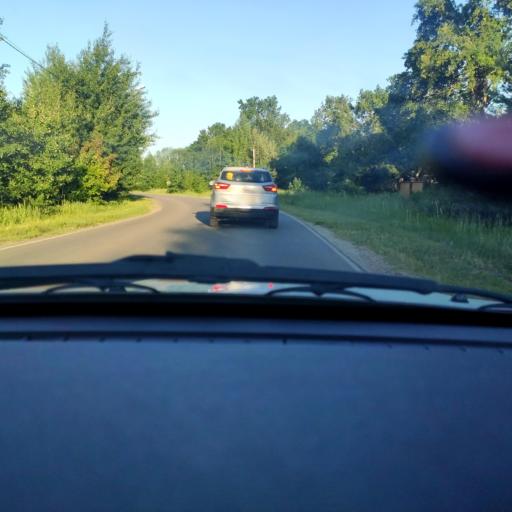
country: RU
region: Voronezj
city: Ramon'
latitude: 51.8911
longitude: 39.2598
